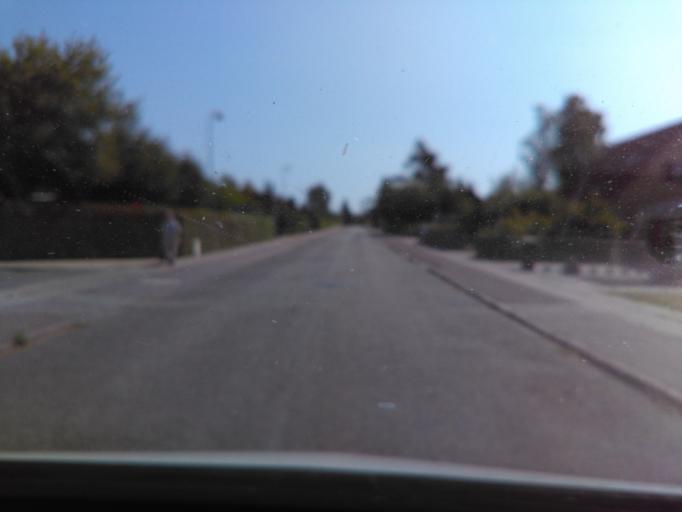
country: DK
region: Capital Region
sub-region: Fureso Kommune
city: Farum
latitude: 55.8124
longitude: 12.3586
